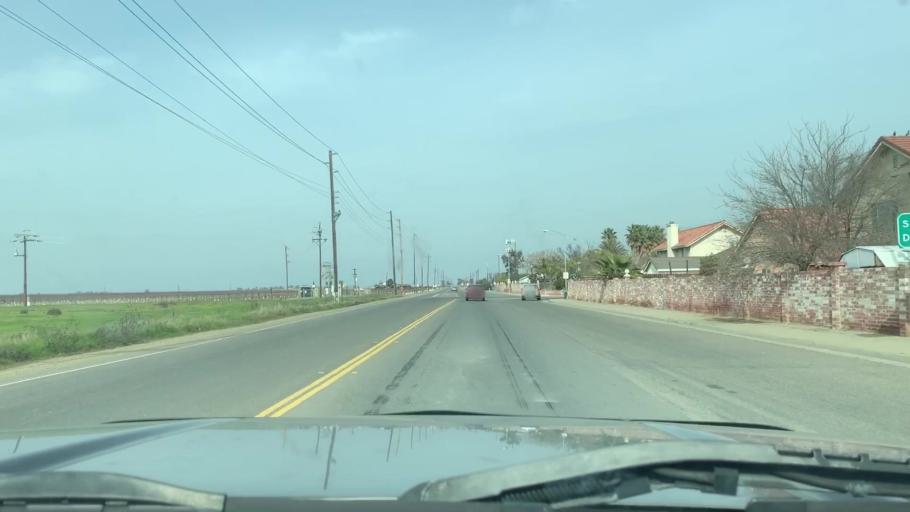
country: US
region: California
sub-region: Merced County
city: Los Banos
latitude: 37.0859
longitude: -120.8349
